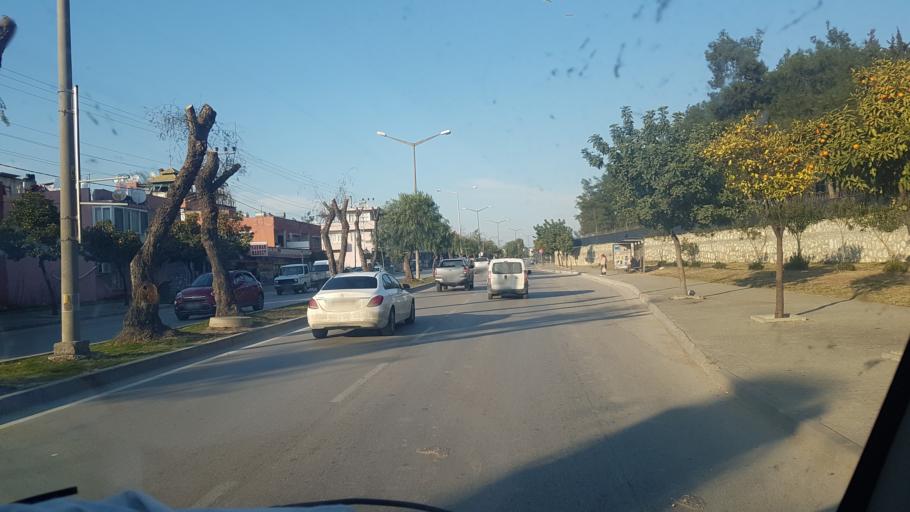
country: TR
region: Adana
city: Adana
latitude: 37.0169
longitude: 35.3403
